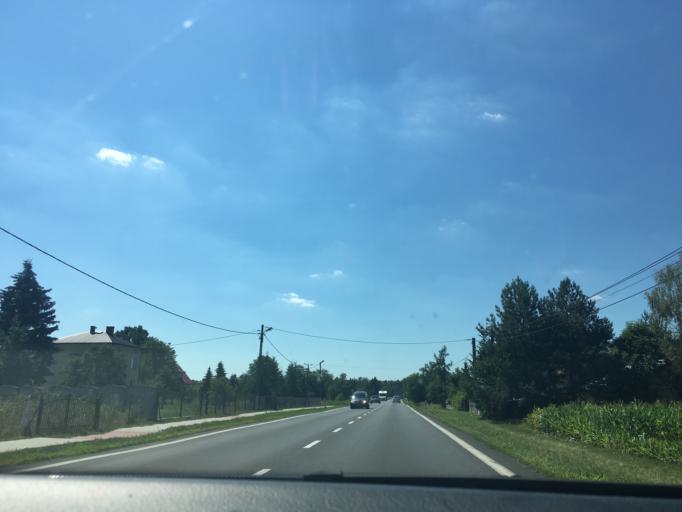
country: PL
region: Subcarpathian Voivodeship
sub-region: Powiat nizanski
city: Nisko
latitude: 50.5035
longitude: 22.1406
